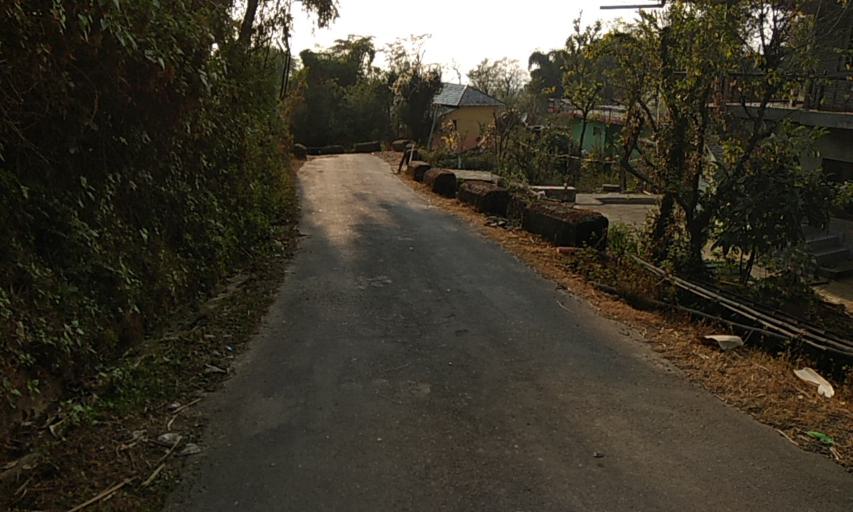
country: IN
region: Himachal Pradesh
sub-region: Kangra
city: Palampur
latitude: 32.1152
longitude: 76.5780
